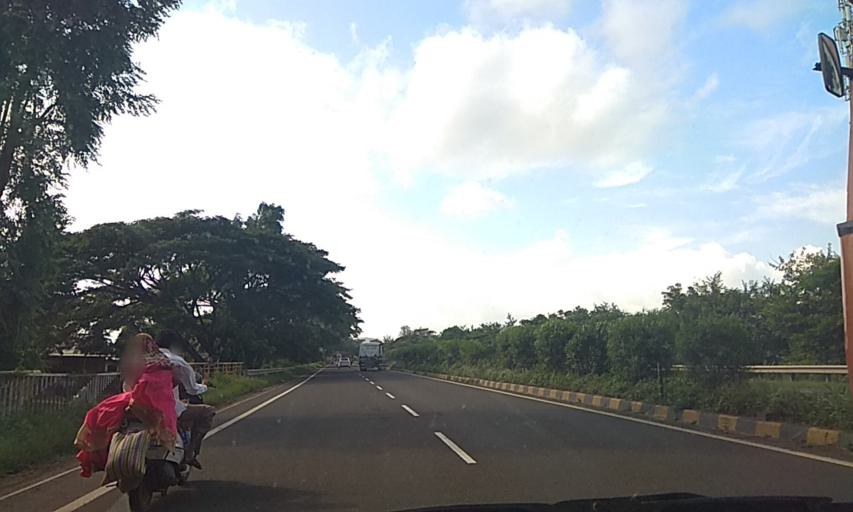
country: IN
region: Maharashtra
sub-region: Kolhapur
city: Kodoli
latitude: 16.9274
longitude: 74.2883
